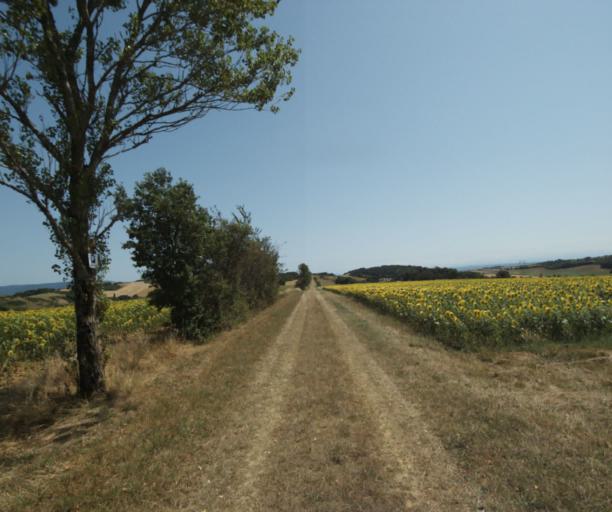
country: FR
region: Midi-Pyrenees
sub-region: Departement de la Haute-Garonne
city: Saint-Felix-Lauragais
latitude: 43.4481
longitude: 1.8599
